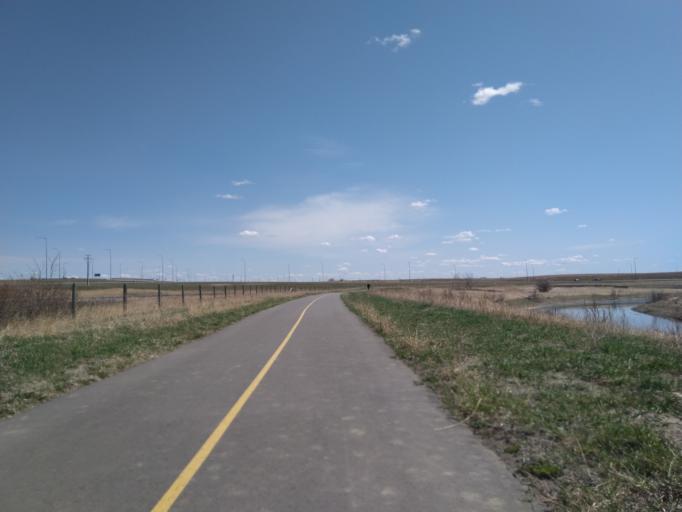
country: CA
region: Alberta
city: Chestermere
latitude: 51.0366
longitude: -113.9273
